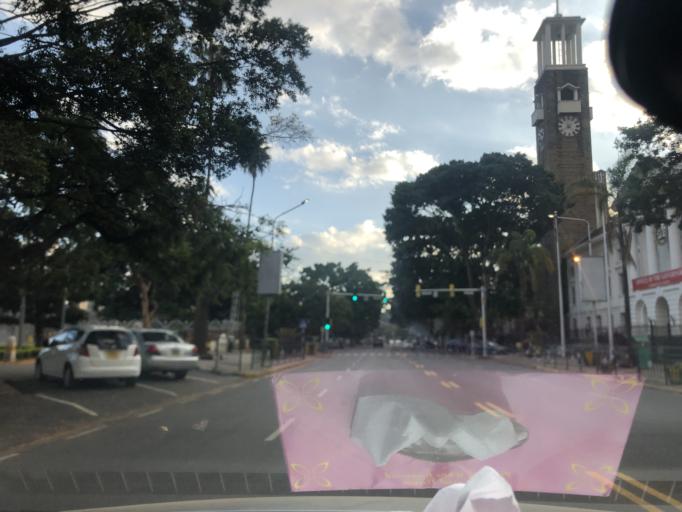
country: KE
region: Nairobi Area
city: Nairobi
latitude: -1.2870
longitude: 36.8223
